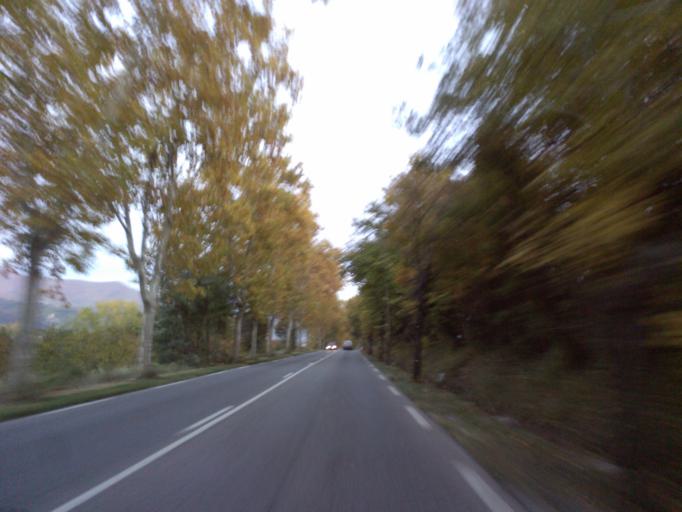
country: FR
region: Provence-Alpes-Cote d'Azur
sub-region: Departement des Alpes-de-Haute-Provence
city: Volonne
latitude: 44.1170
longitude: 5.9920
